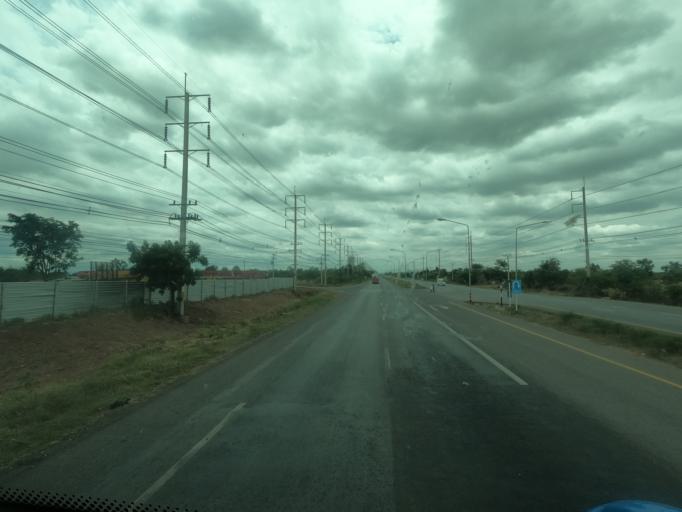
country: TH
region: Nakhon Ratchasima
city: Chok Chai
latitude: 14.7384
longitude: 102.1292
